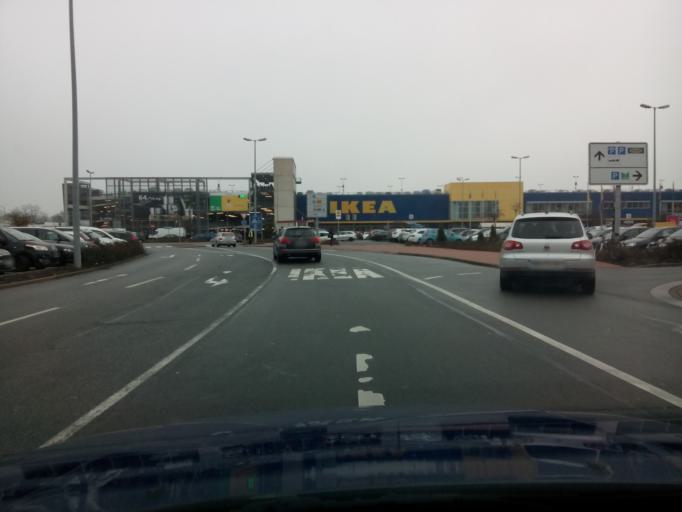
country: DE
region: Bremen
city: Bremen
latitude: 53.0276
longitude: 8.8014
